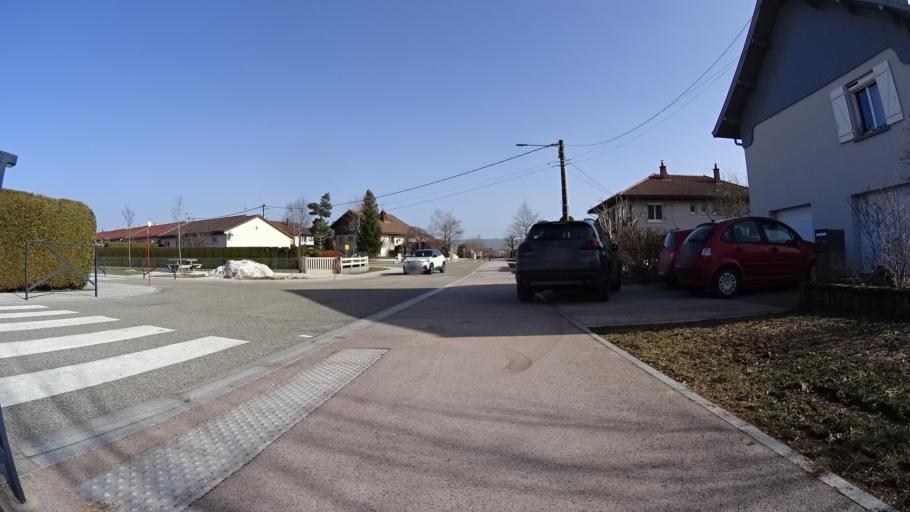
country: FR
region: Franche-Comte
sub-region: Departement du Doubs
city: Frasne
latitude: 46.8505
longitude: 6.1567
